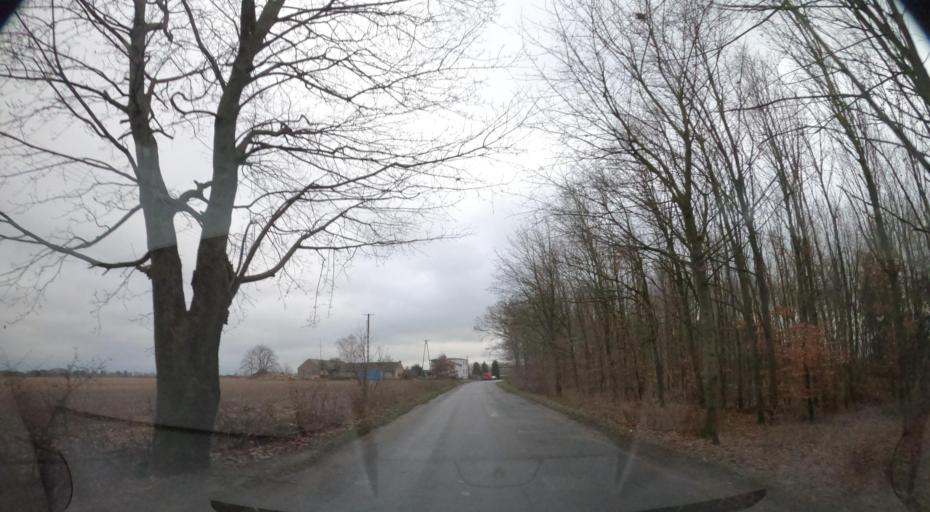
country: PL
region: Greater Poland Voivodeship
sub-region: Powiat pilski
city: Lobzenica
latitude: 53.2389
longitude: 17.3038
